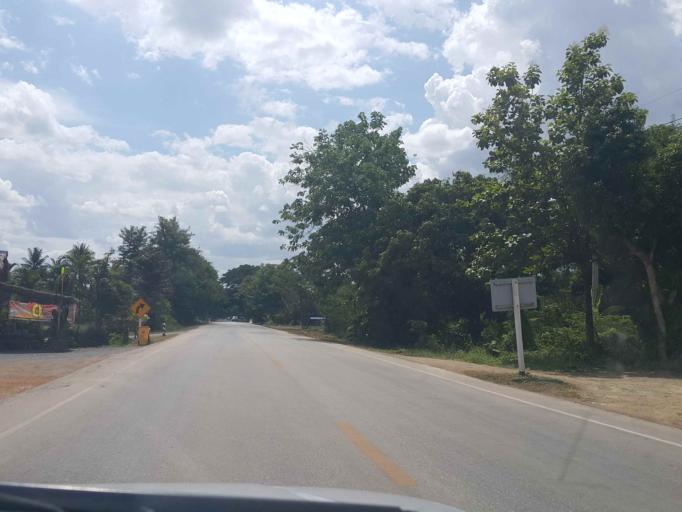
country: TH
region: Sukhothai
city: Thung Saliam
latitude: 17.3290
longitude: 99.6257
